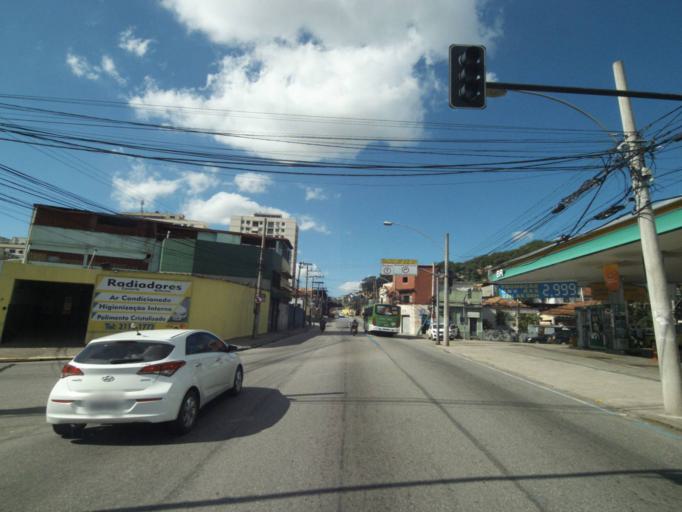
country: BR
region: Rio de Janeiro
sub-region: Rio De Janeiro
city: Rio de Janeiro
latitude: -22.9050
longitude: -43.2673
